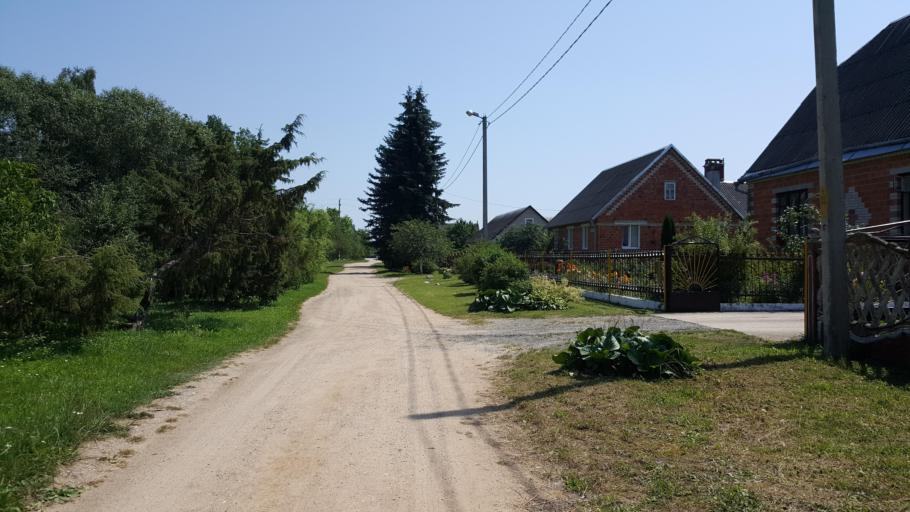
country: BY
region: Brest
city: Zhabinka
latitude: 52.1919
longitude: 23.9987
